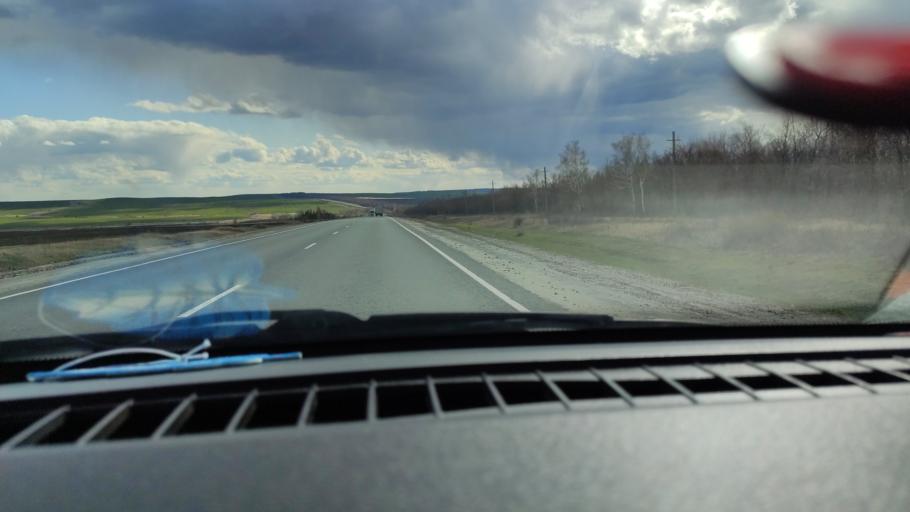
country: RU
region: Saratov
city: Alekseyevka
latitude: 52.2587
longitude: 47.9189
